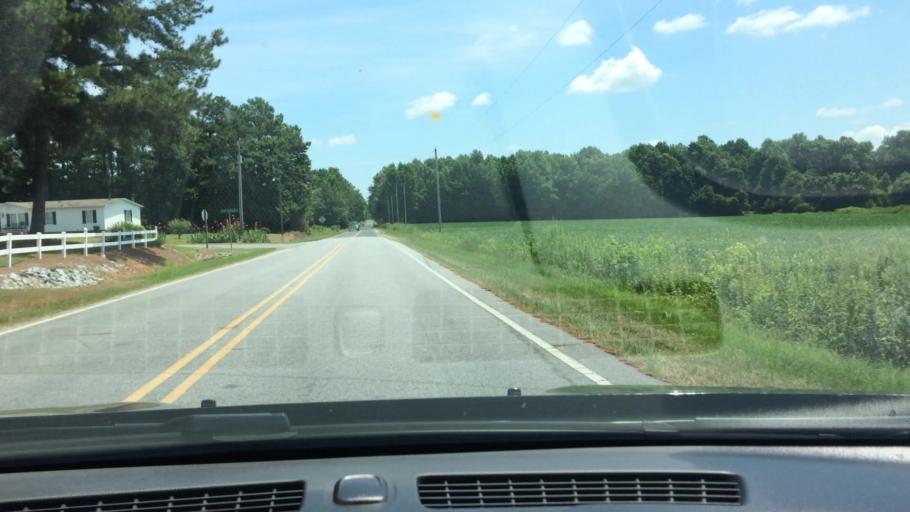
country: US
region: North Carolina
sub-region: Pitt County
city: Ayden
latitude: 35.4878
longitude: -77.3725
